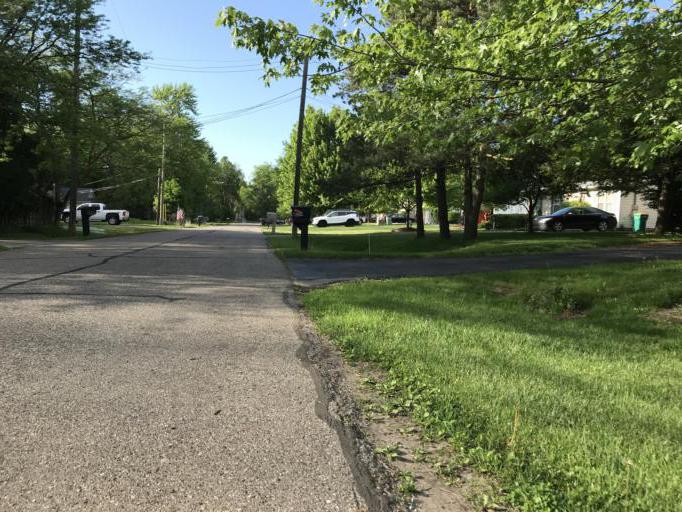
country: US
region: Michigan
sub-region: Oakland County
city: Farmington
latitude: 42.4625
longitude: -83.3312
